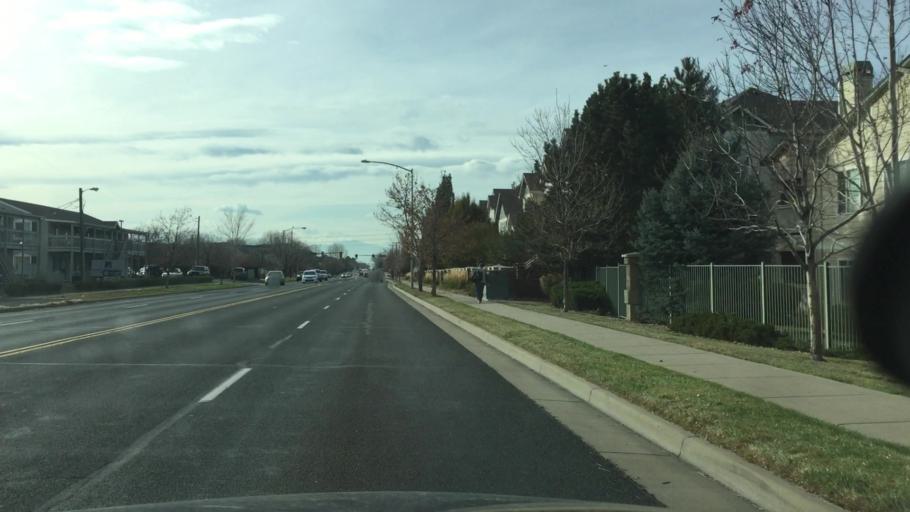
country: US
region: Colorado
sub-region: Adams County
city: Aurora
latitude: 39.6893
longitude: -104.8726
